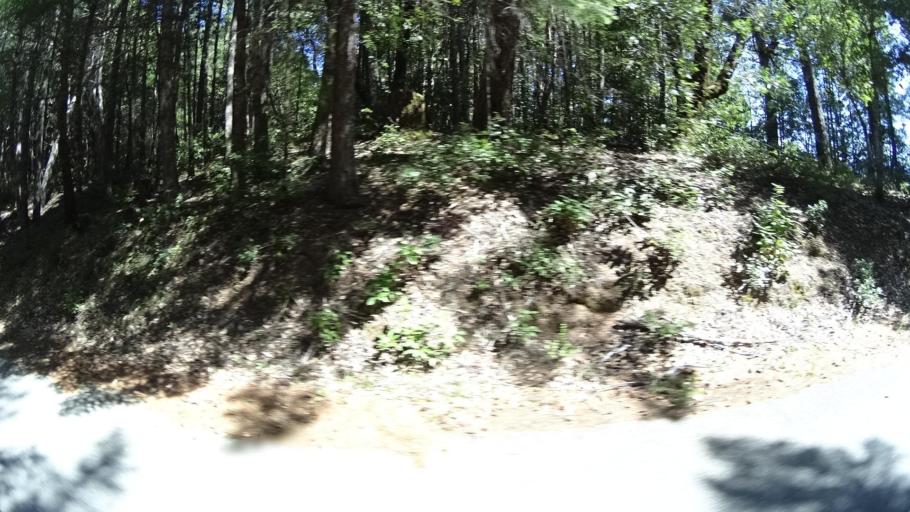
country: US
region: California
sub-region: Humboldt County
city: Redway
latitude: 40.1958
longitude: -124.0970
